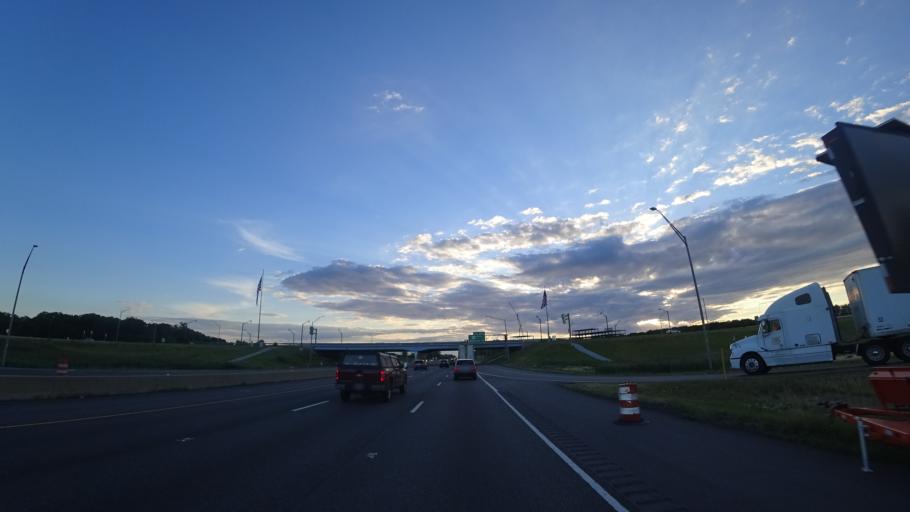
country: US
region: Indiana
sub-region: LaPorte County
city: Michigan City
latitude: 41.6584
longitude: -86.8922
